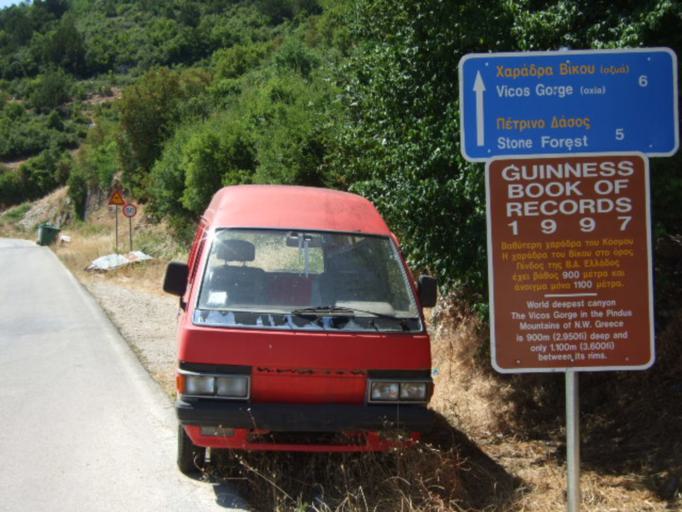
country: GR
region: Epirus
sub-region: Nomos Ioanninon
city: Asprangeloi
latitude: 39.8834
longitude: 20.7449
